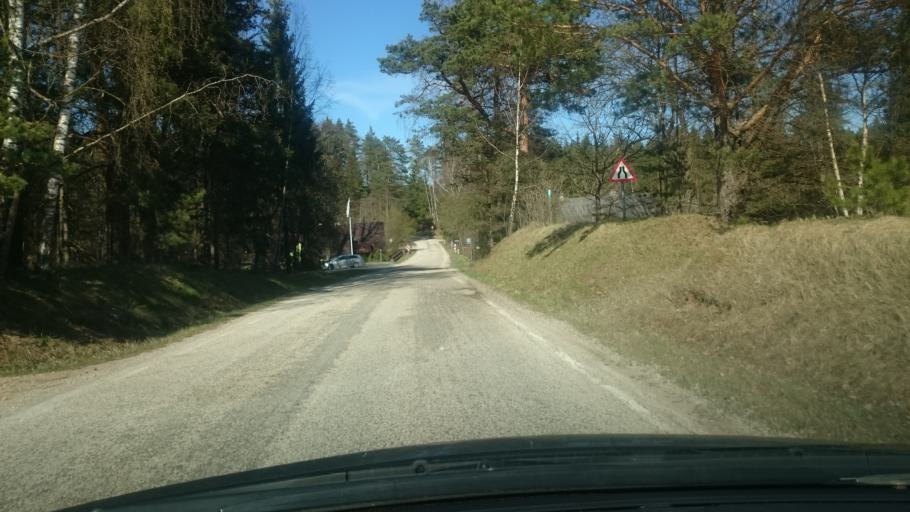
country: EE
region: Polvamaa
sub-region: Polva linn
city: Polva
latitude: 58.1386
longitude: 27.0182
